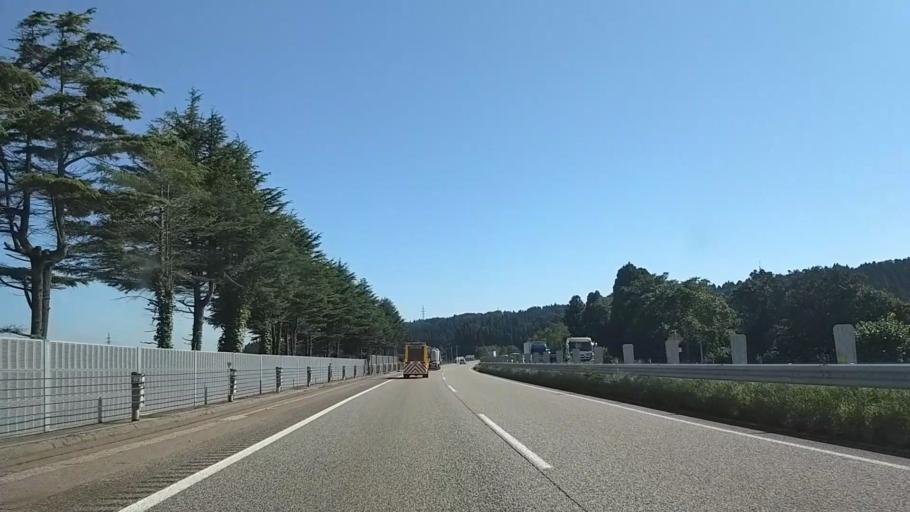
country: JP
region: Toyama
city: Takaoka
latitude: 36.6795
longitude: 137.0395
